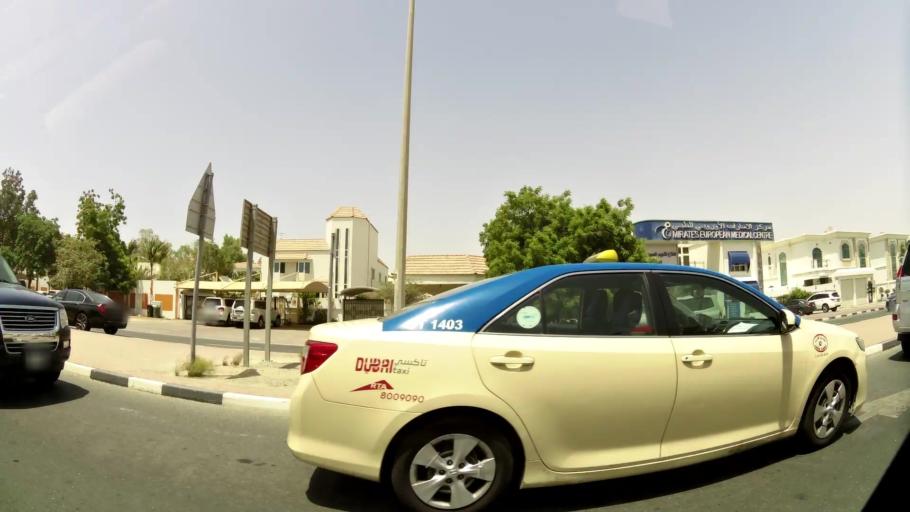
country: AE
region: Dubai
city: Dubai
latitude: 25.1410
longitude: 55.2033
